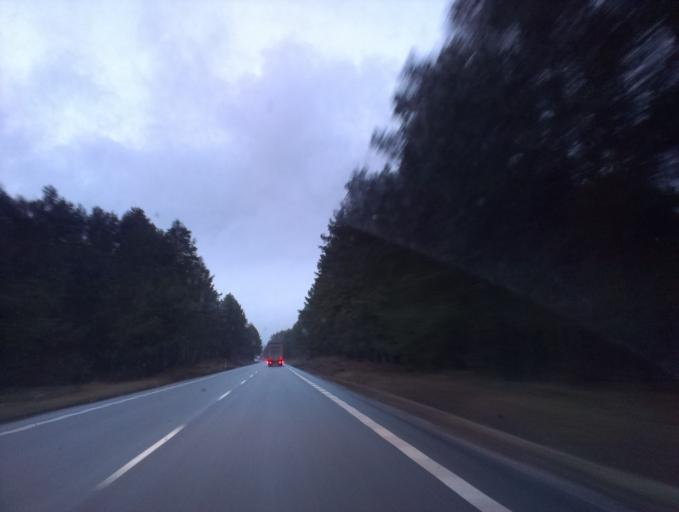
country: PL
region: Swietokrzyskie
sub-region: Powiat konecki
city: Ruda Maleniecka
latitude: 51.1942
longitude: 20.2105
